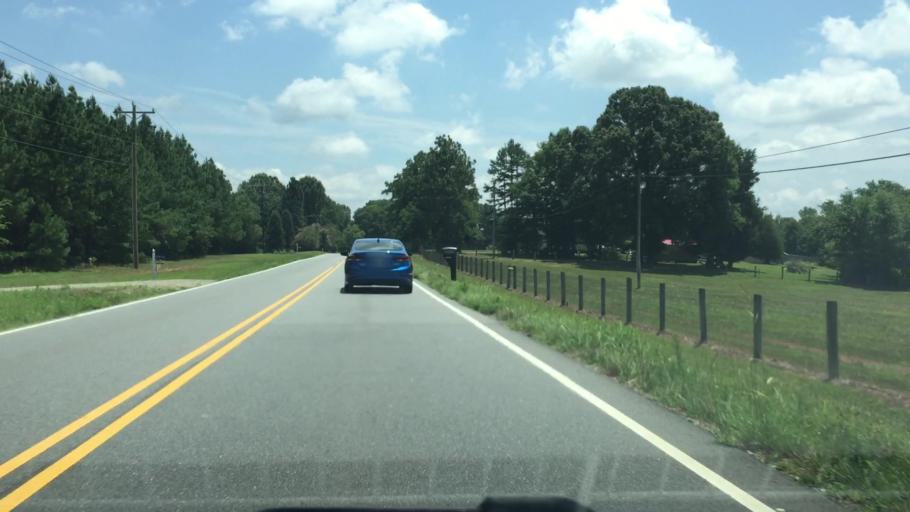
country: US
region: North Carolina
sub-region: Rowan County
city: Enochville
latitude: 35.4669
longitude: -80.7413
